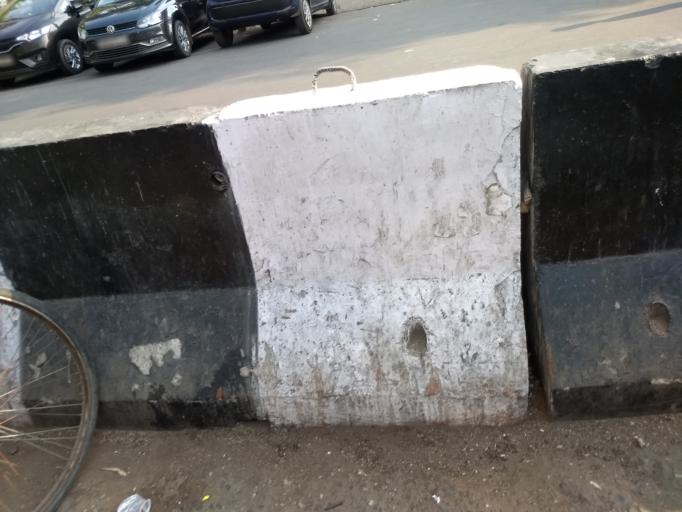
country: IN
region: NCT
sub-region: New Delhi
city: New Delhi
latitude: 28.5678
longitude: 77.2433
